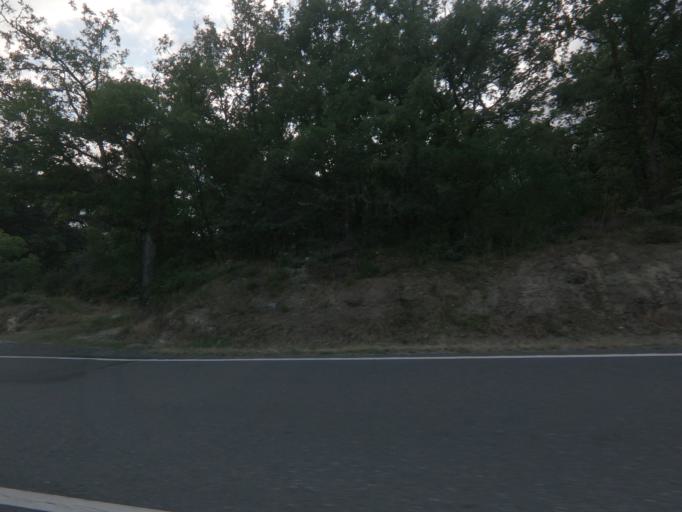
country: ES
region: Galicia
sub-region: Provincia de Ourense
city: Taboadela
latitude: 42.2505
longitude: -7.8373
